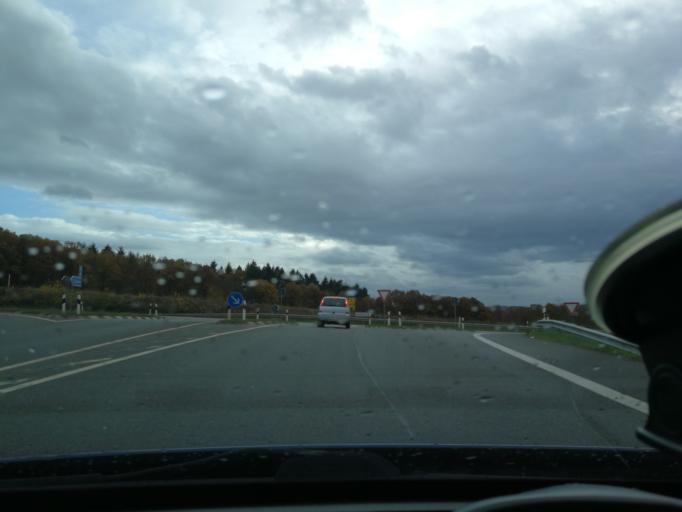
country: DE
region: Rheinland-Pfalz
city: Esch
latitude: 49.9016
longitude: 6.8549
